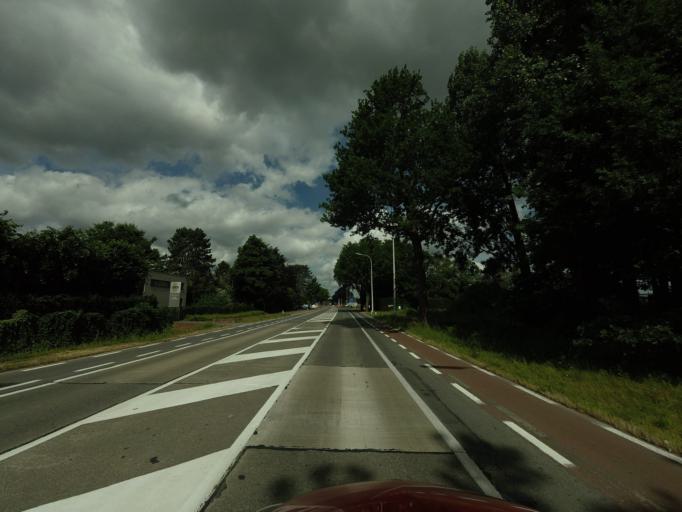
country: BE
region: Flanders
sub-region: Provincie Oost-Vlaanderen
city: Eeklo
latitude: 51.1963
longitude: 3.5392
